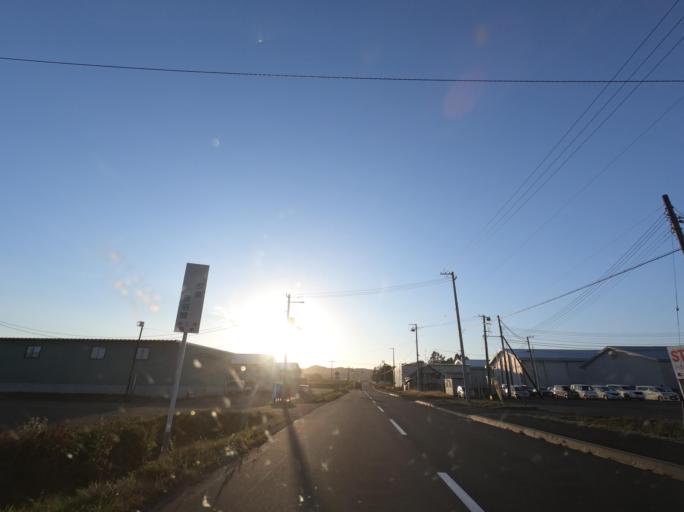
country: JP
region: Hokkaido
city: Chitose
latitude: 42.9741
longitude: 141.7930
